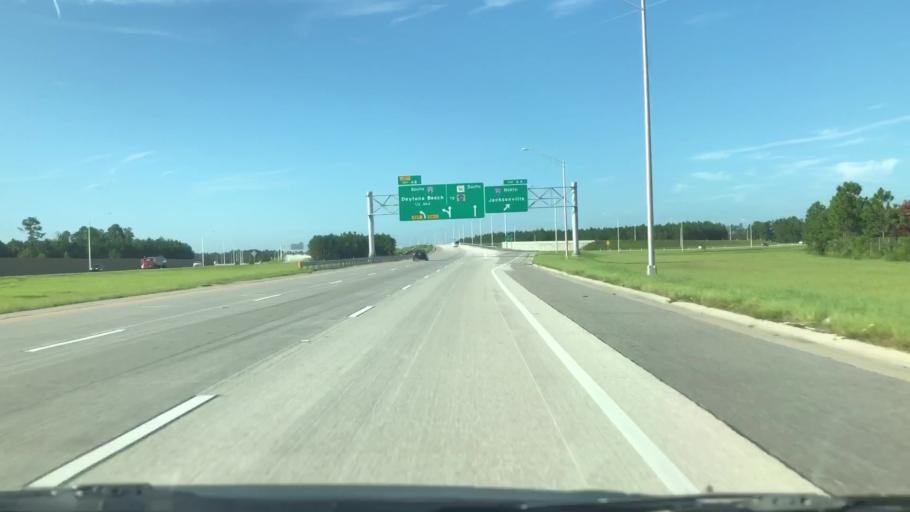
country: US
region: Florida
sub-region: Saint Johns County
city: Fruit Cove
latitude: 30.1230
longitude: -81.5125
